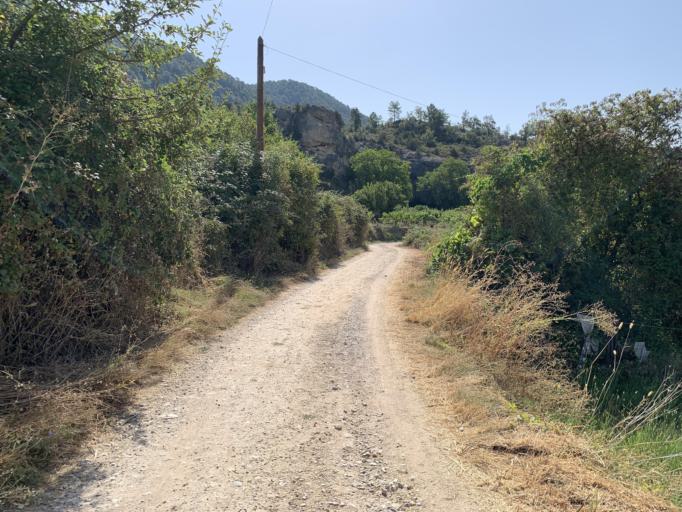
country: ES
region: Castille-La Mancha
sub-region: Provincia de Guadalajara
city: Ocentejo
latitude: 40.7701
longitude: -2.3974
